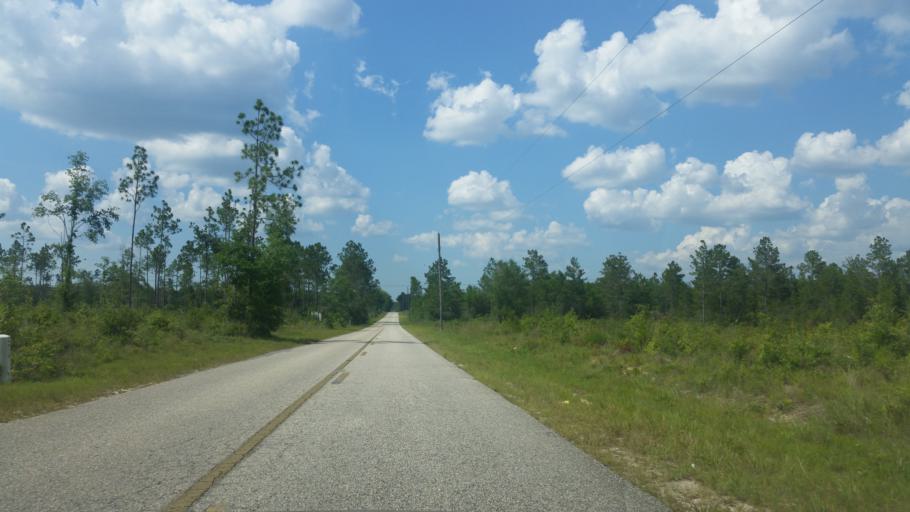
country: US
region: Florida
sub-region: Santa Rosa County
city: East Milton
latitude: 30.6641
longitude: -86.8788
